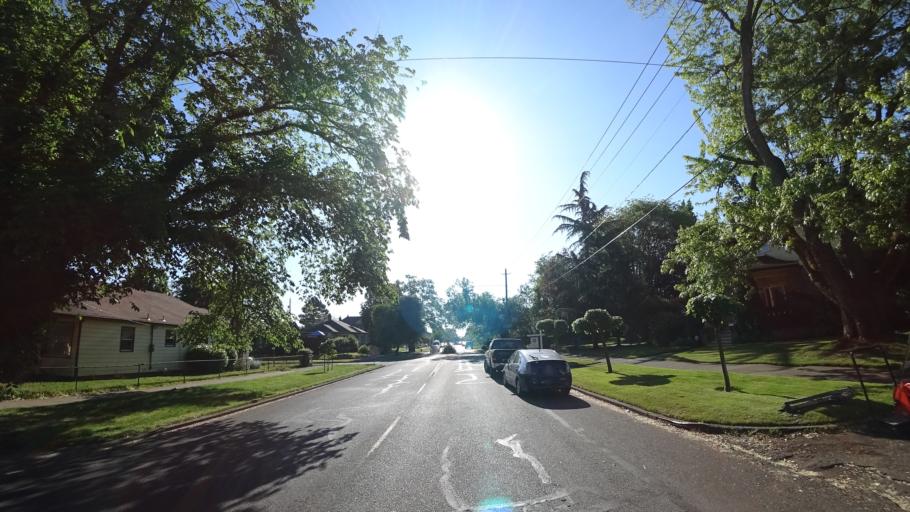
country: US
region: Oregon
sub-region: Multnomah County
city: Portland
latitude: 45.5664
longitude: -122.6644
